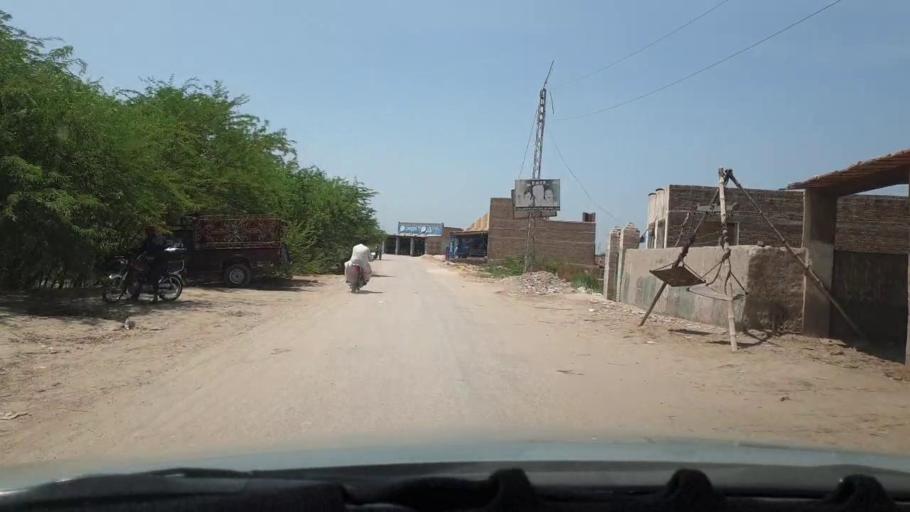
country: PK
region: Sindh
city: Pano Aqil
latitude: 27.6626
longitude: 69.1636
